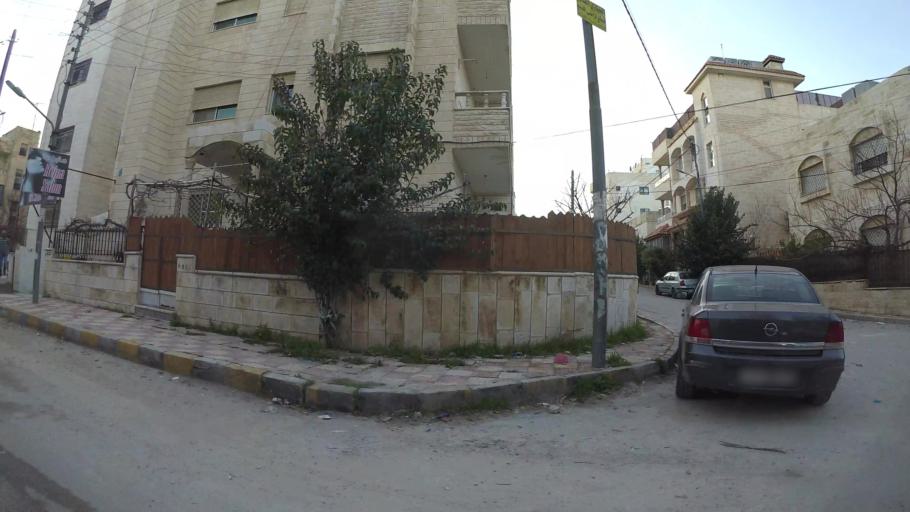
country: JO
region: Amman
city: Al Bunayyat ash Shamaliyah
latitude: 31.9170
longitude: 35.8951
